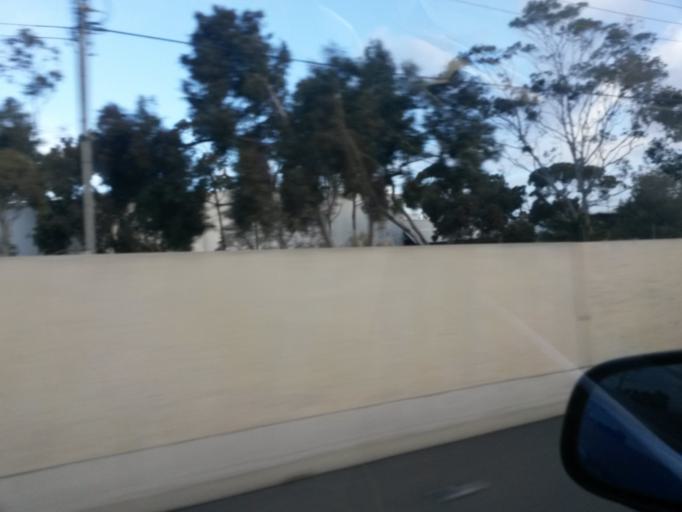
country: AU
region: South Australia
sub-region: Port Adelaide Enfield
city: Alberton
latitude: -34.8395
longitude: 138.5199
